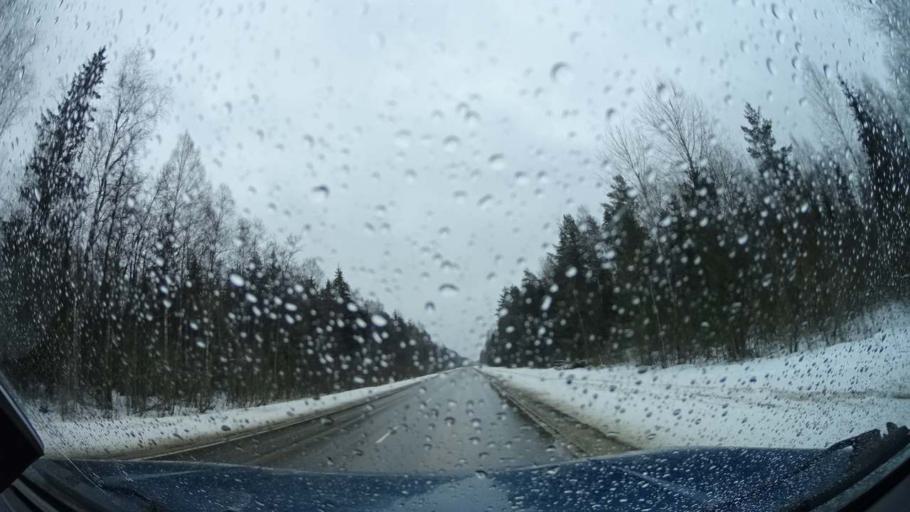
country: RU
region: Tverskaya
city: Gorodnya
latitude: 56.8490
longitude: 36.4032
